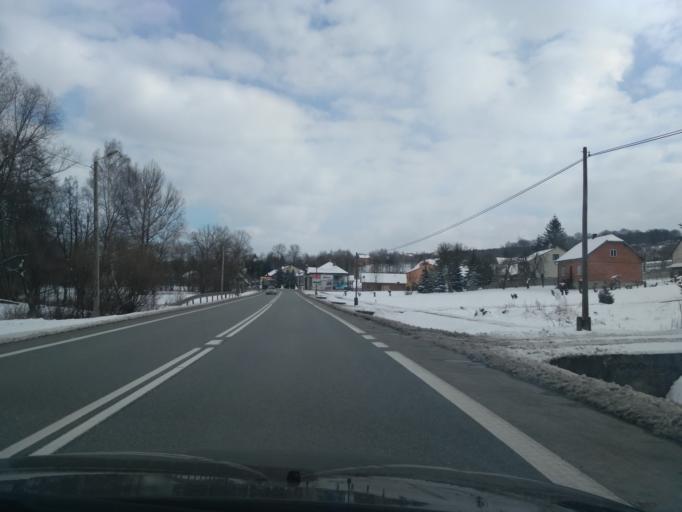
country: PL
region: Subcarpathian Voivodeship
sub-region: Powiat strzyzowski
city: Polomia
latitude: 49.9005
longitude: 21.8715
